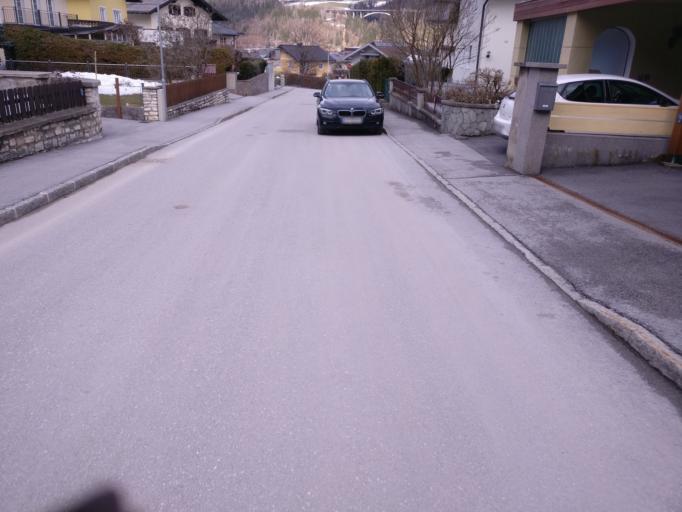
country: AT
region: Salzburg
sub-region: Politischer Bezirk Sankt Johann im Pongau
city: Bischofshofen
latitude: 47.4192
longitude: 13.2137
